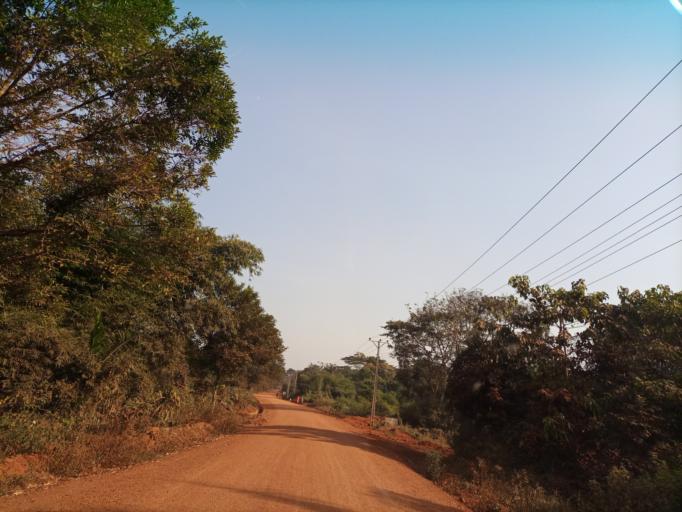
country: NG
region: Enugu
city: Opi
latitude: 6.7566
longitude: 7.4038
